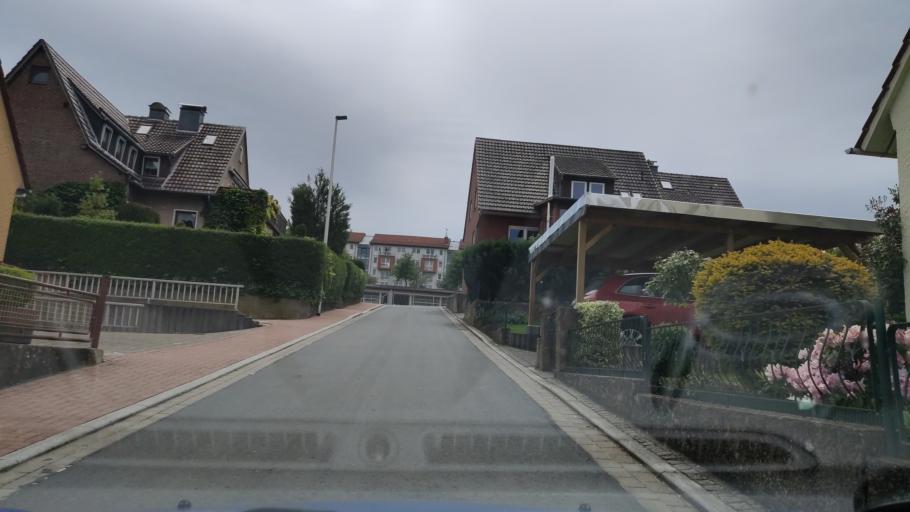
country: DE
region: Lower Saxony
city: Uslar
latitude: 51.6545
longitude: 9.6368
